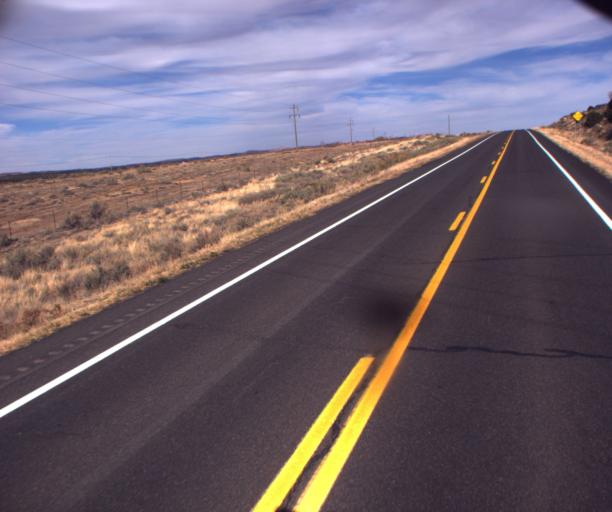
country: US
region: Arizona
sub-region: Navajo County
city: Kayenta
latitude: 36.6730
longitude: -110.3996
